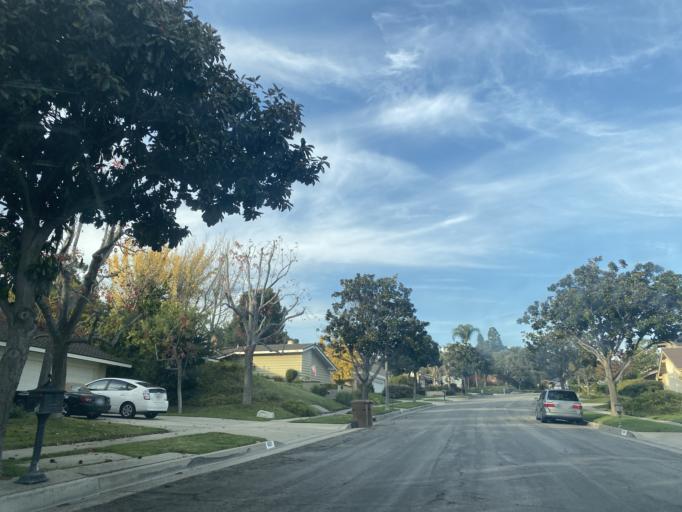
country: US
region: California
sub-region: Orange County
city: Placentia
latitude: 33.8859
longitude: -117.8957
